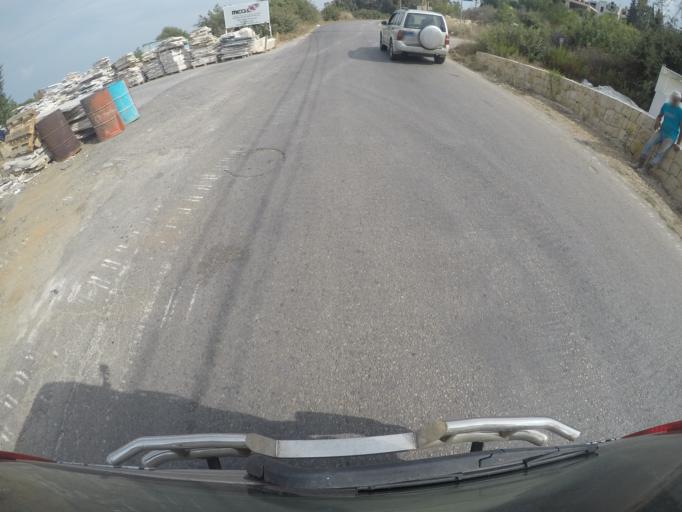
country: LB
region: Mont-Liban
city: Beit ed Dine
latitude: 33.7356
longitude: 35.4788
